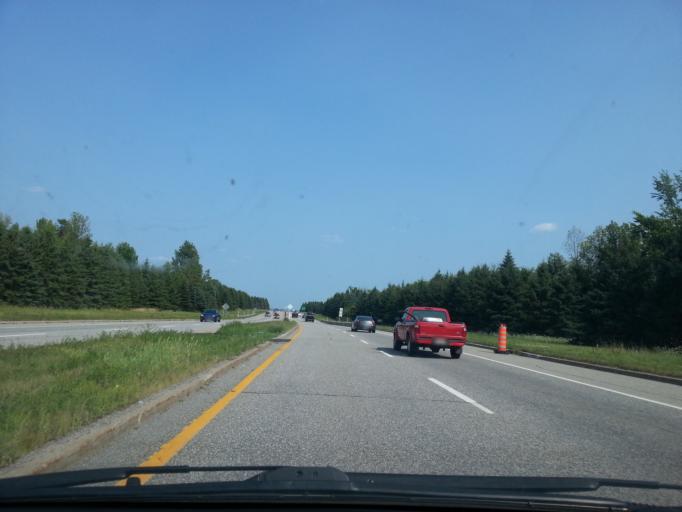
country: CA
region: Quebec
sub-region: Outaouais
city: Gatineau
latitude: 45.4714
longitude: -75.7675
